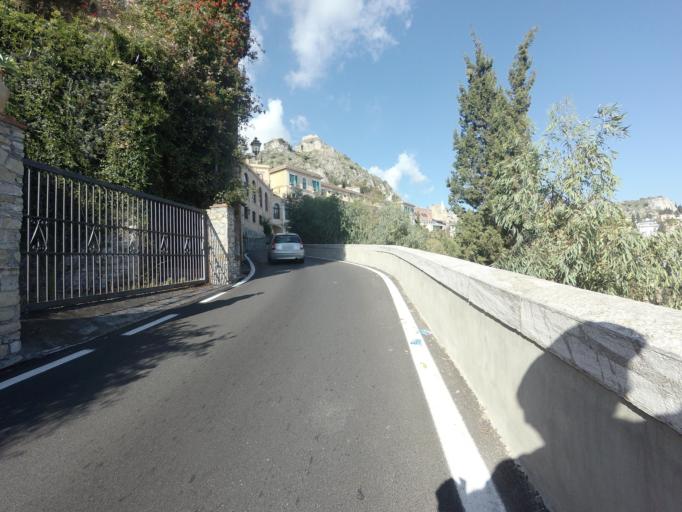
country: IT
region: Sicily
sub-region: Messina
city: Taormina
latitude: 37.8495
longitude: 15.2840
